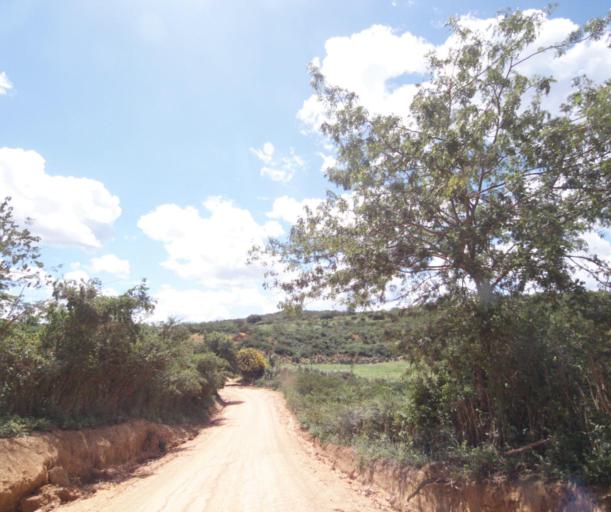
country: BR
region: Bahia
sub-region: Pocoes
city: Pocoes
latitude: -14.2991
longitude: -40.6447
